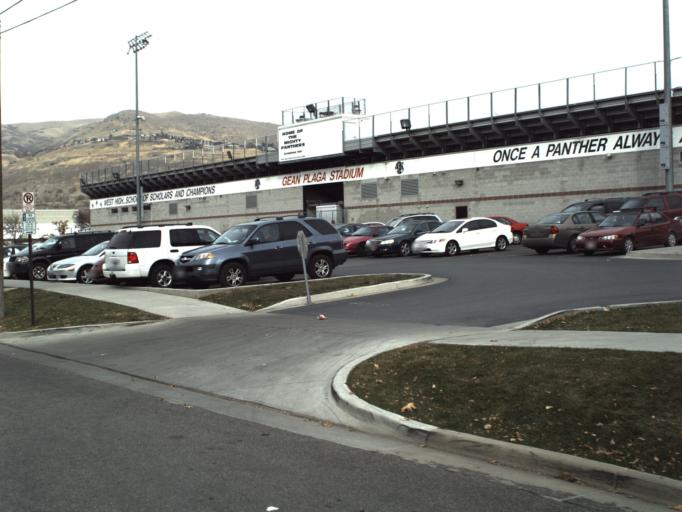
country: US
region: Utah
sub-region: Salt Lake County
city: Salt Lake City
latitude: 40.7746
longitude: -111.9024
